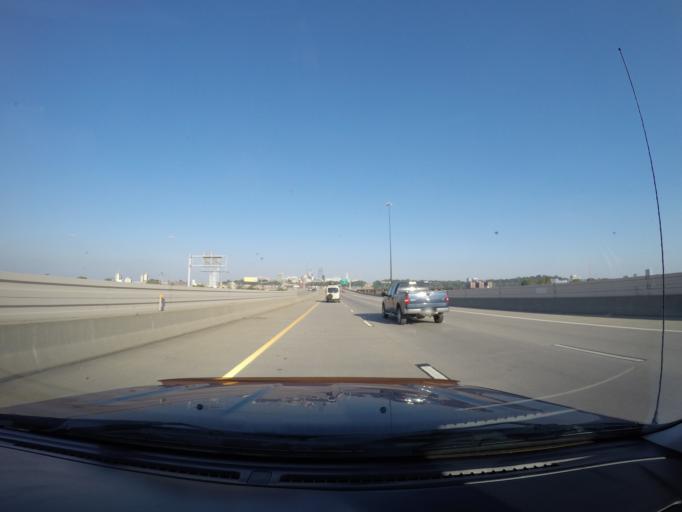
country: US
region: Kansas
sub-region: Wyandotte County
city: Kansas City
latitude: 39.0988
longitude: -94.6155
